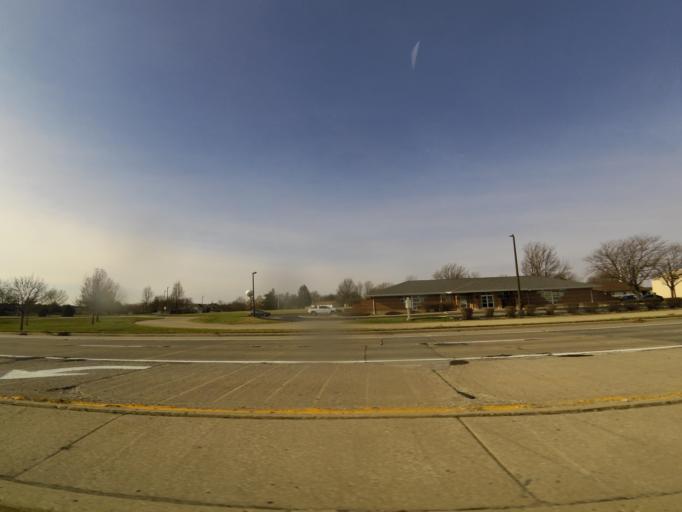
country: US
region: Illinois
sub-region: Macon County
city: Forsyth
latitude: 39.9330
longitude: -88.9556
